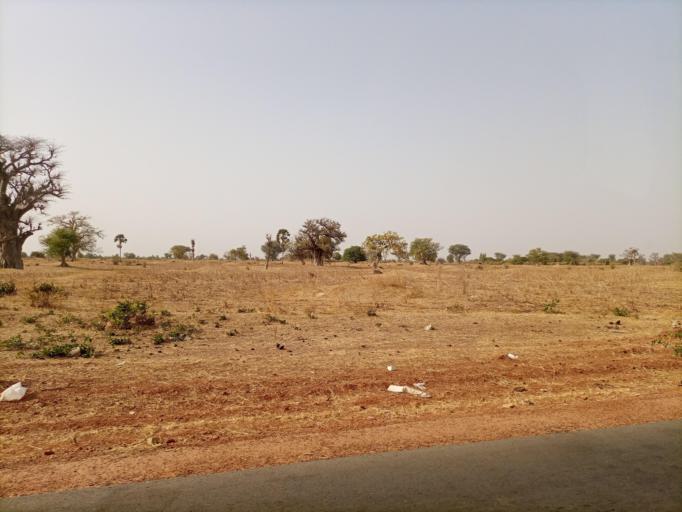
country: SN
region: Fatick
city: Foundiougne
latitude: 14.1229
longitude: -16.4281
